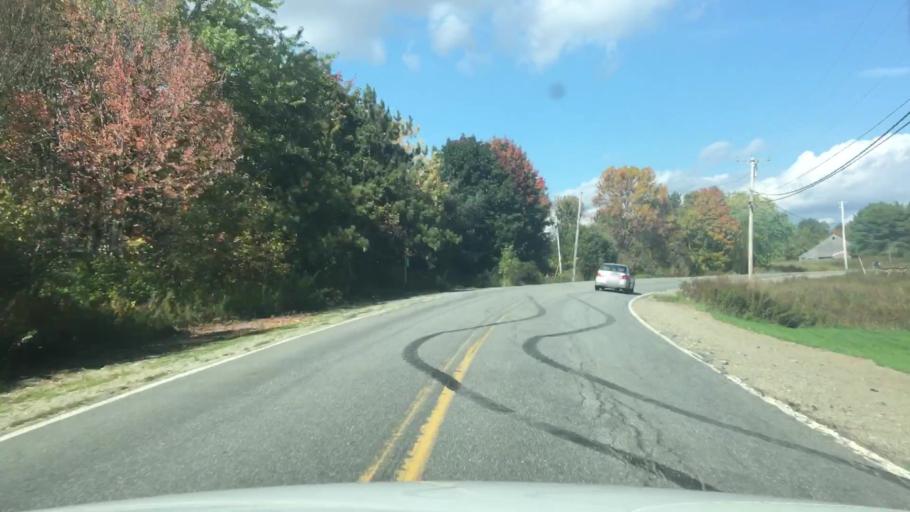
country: US
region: Maine
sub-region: Knox County
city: Warren
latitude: 44.1386
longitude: -69.2366
